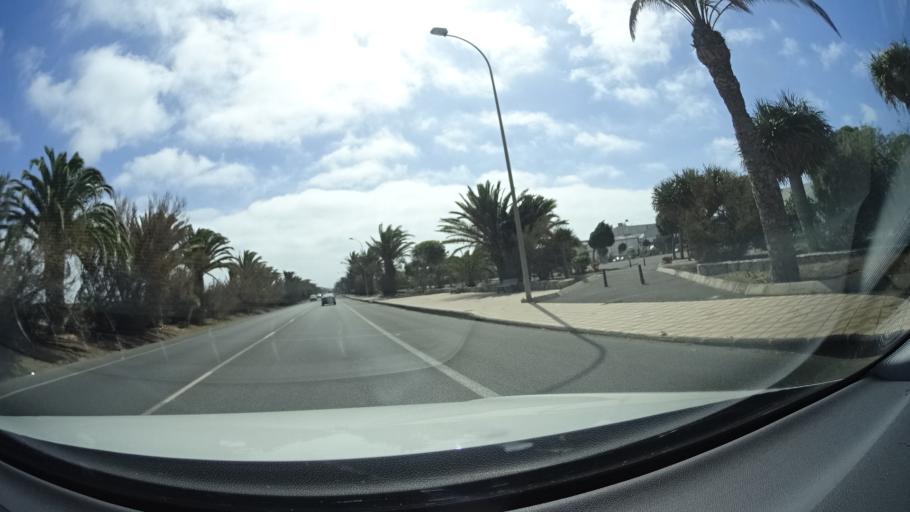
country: ES
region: Canary Islands
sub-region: Provincia de Las Palmas
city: Cruce de Arinaga
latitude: 27.8613
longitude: -15.4027
